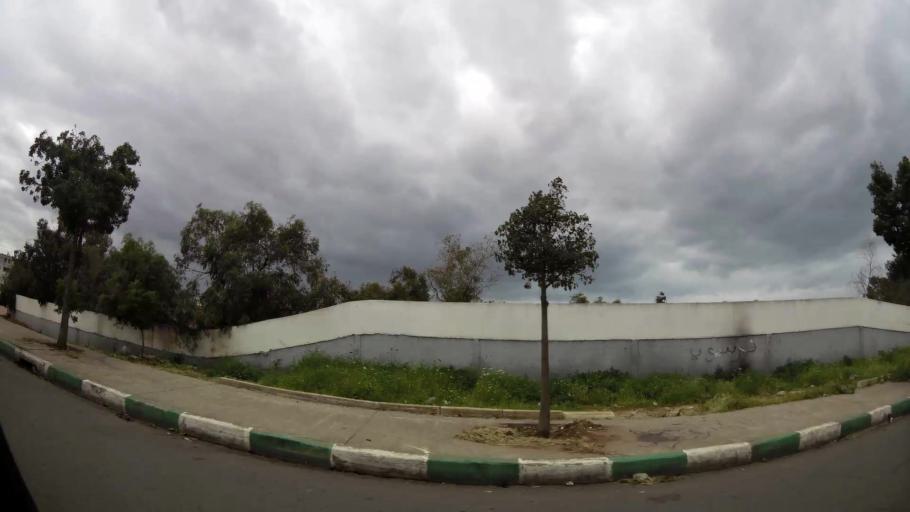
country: MA
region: Grand Casablanca
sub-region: Casablanca
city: Casablanca
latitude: 33.5936
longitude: -7.5516
